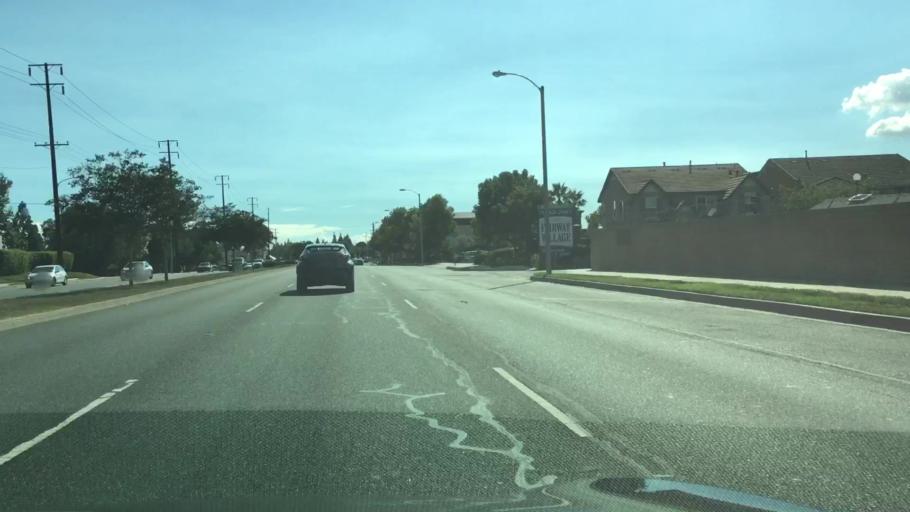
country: US
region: California
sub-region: Orange County
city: Buena Park
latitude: 33.8873
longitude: -117.9937
